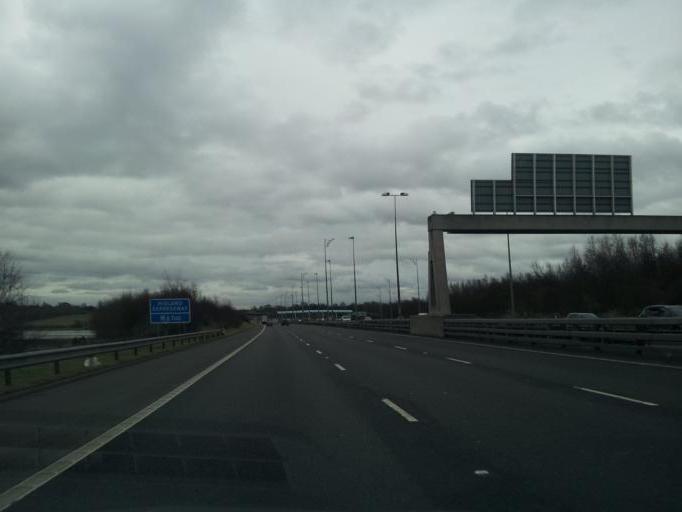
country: GB
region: England
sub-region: Staffordshire
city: Great Wyrley
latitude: 52.6702
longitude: -2.0055
